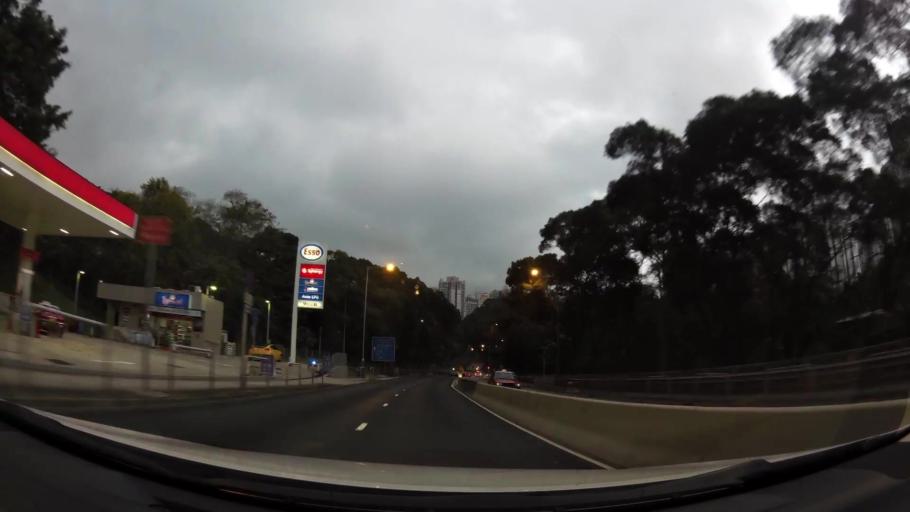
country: HK
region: Tsuen Wan
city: Tsuen Wan
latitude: 22.3568
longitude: 114.1005
